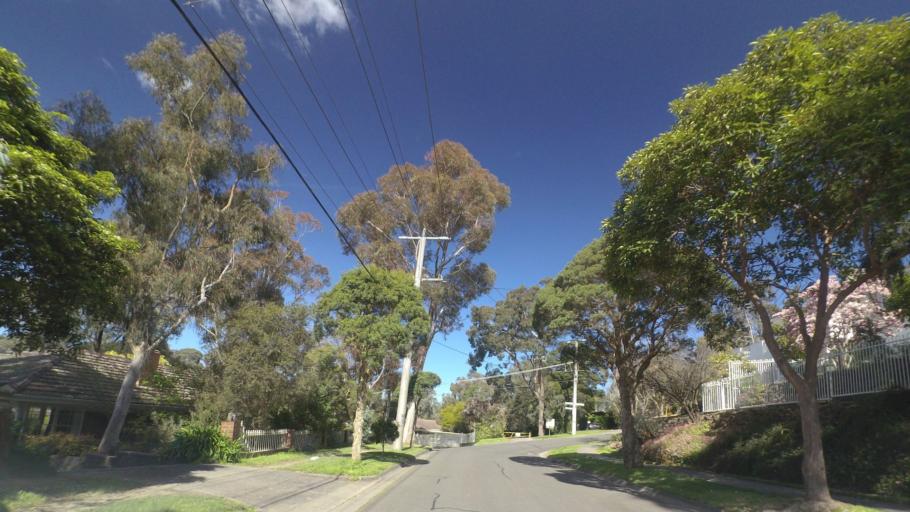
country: AU
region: Victoria
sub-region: Maroondah
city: Heathmont
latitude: -37.8367
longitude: 145.2443
